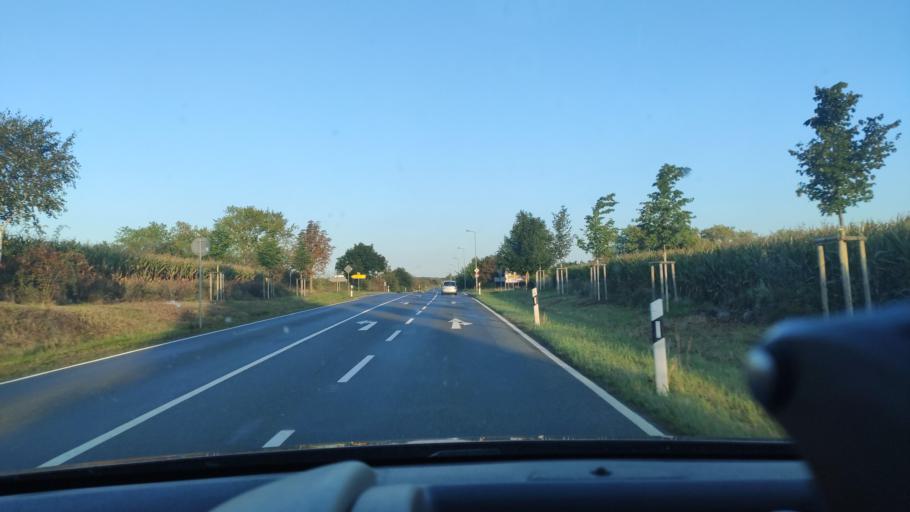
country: DE
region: Mecklenburg-Vorpommern
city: Lalendorf
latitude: 53.6206
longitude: 12.4271
